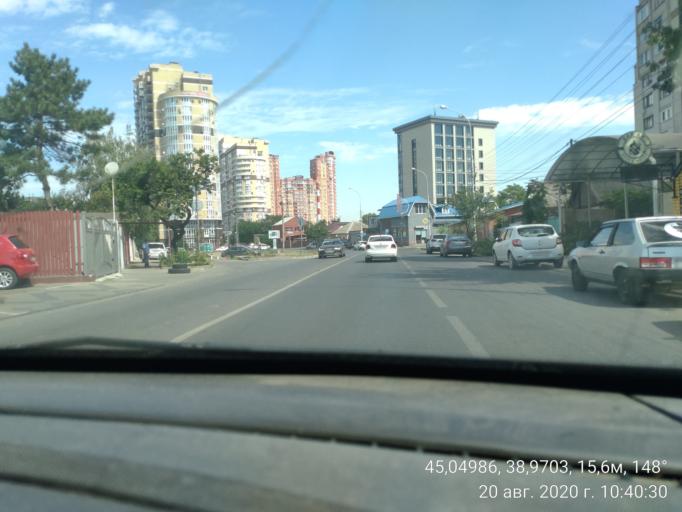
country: RU
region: Krasnodarskiy
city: Krasnodar
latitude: 45.0499
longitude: 38.9702
